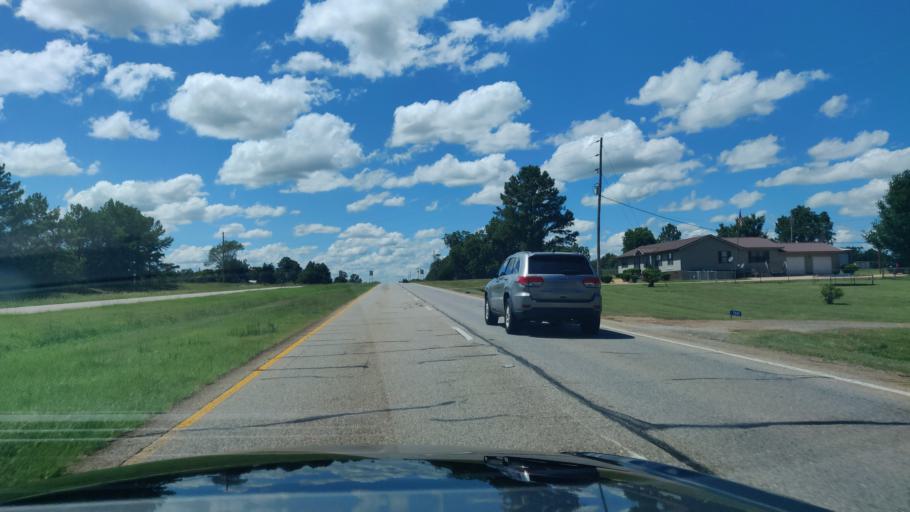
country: US
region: Georgia
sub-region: Webster County
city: Preston
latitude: 31.9305
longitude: -84.5587
